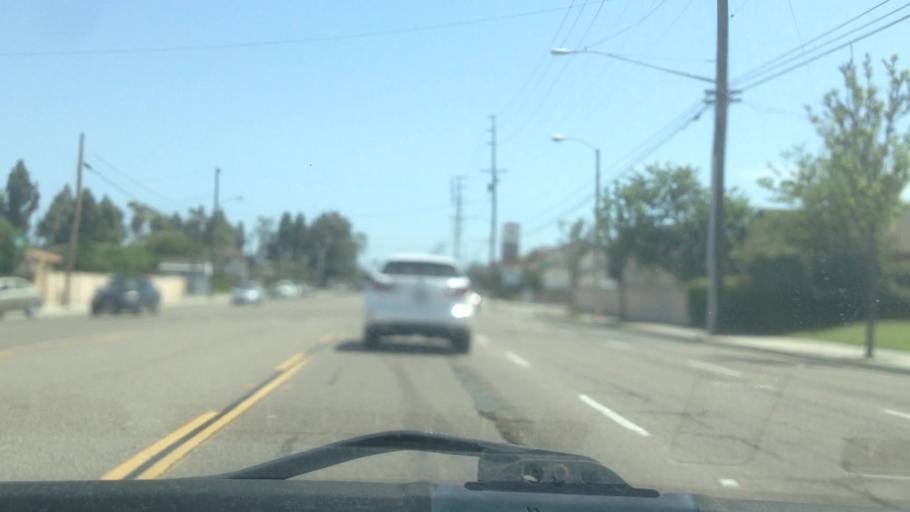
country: US
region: California
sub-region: Orange County
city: Garden Grove
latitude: 33.7403
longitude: -117.9374
